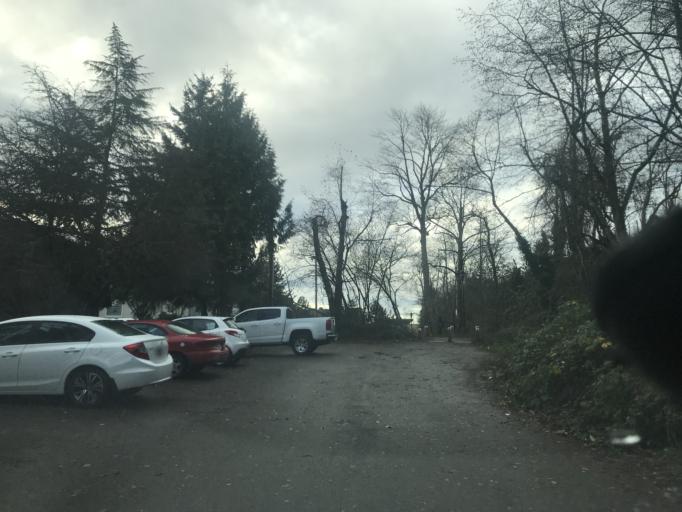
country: US
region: Washington
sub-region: King County
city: White Center
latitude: 47.5258
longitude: -122.3658
